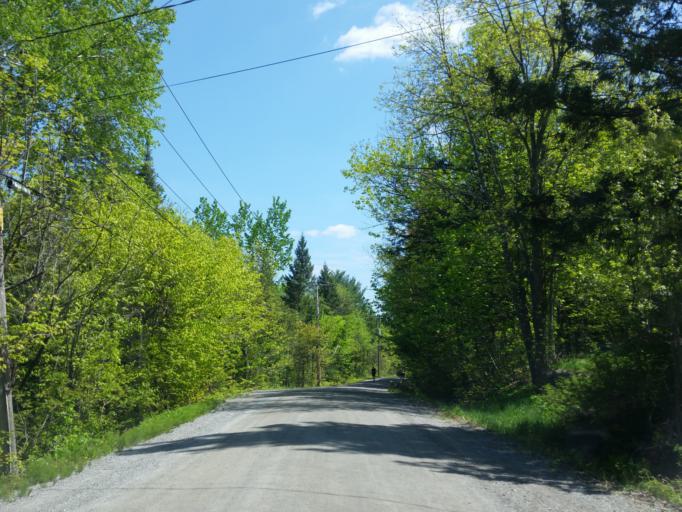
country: CA
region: Quebec
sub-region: Outaouais
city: Wakefield
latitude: 45.5786
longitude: -75.8748
